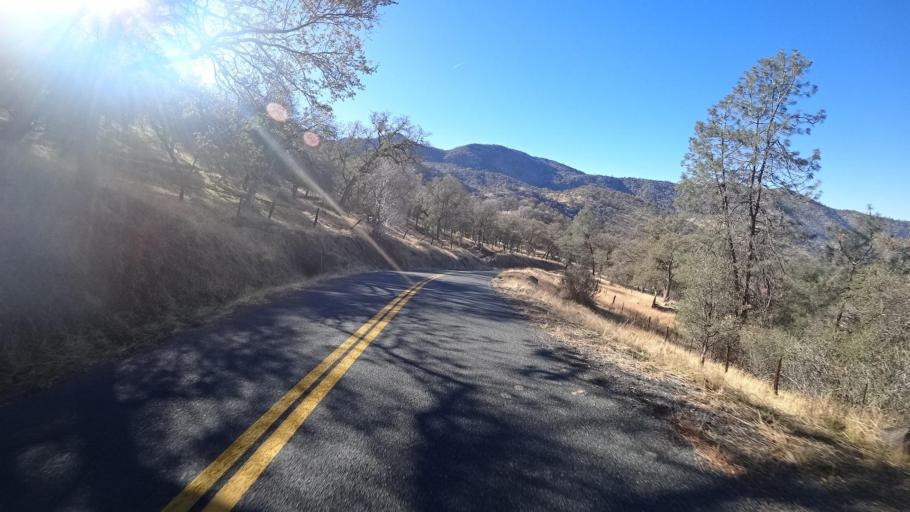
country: US
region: California
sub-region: Kern County
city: Alta Sierra
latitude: 35.7868
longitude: -118.7699
